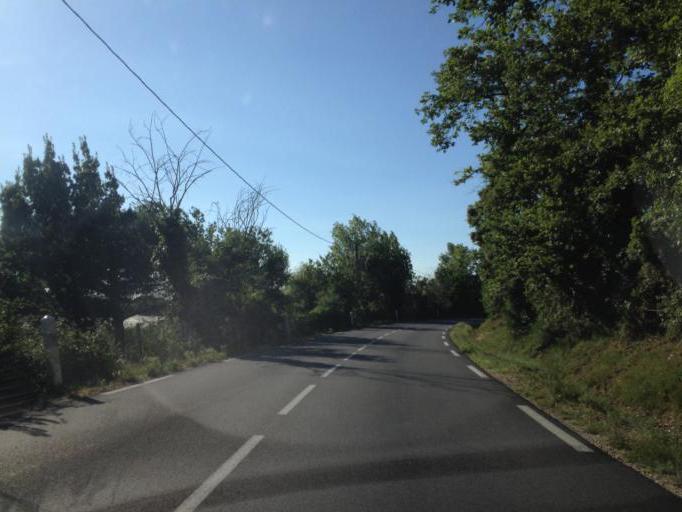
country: FR
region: Languedoc-Roussillon
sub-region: Departement du Gard
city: Montfaucon
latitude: 44.0763
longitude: 4.7800
